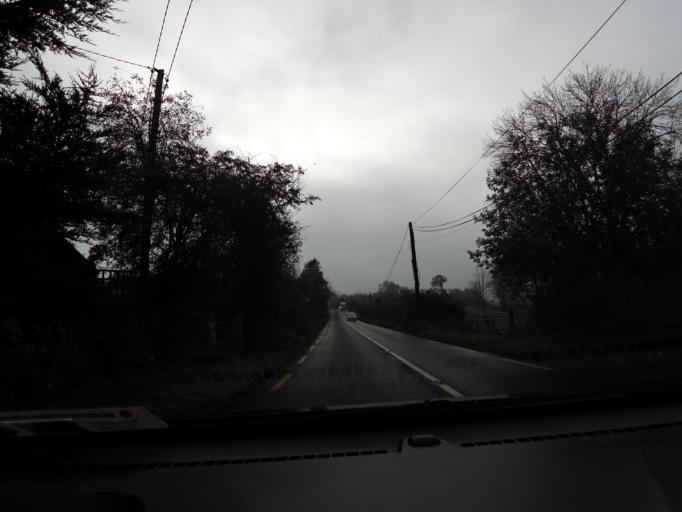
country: IE
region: Leinster
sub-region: An Iarmhi
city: Athlone
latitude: 53.4014
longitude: -7.8786
